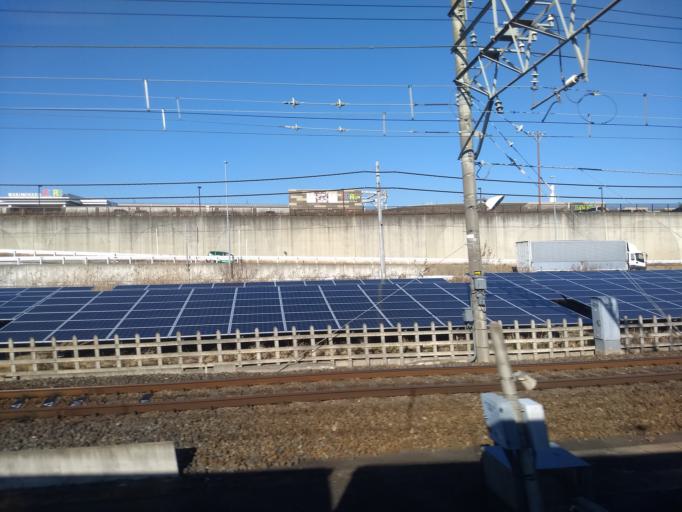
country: JP
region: Ibaraki
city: Ryugasaki
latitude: 35.8041
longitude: 140.1644
